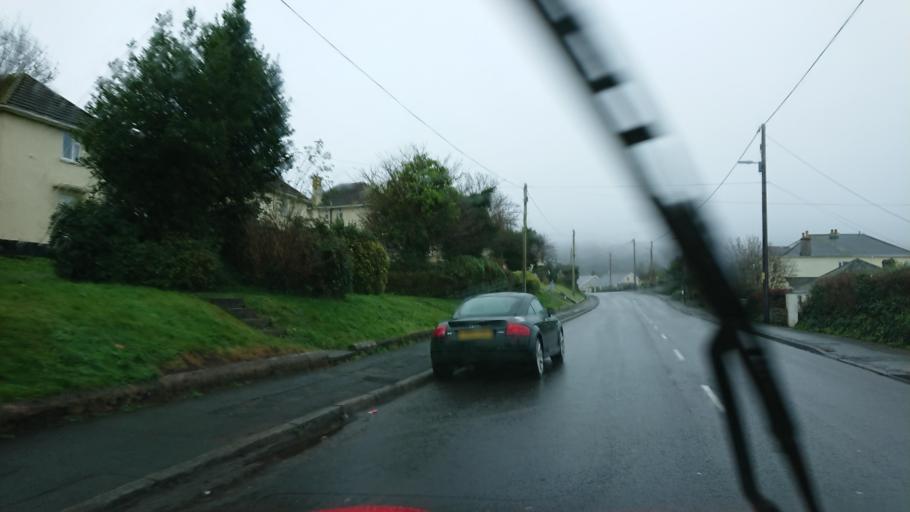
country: GB
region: England
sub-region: Plymouth
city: Plymstock
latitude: 50.3560
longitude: -4.0993
